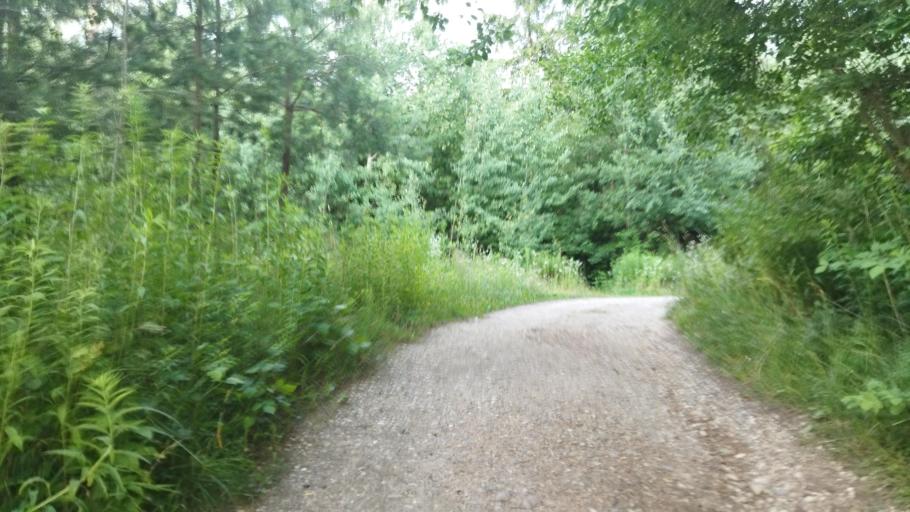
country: DE
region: Bavaria
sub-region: Upper Palatinate
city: Mintraching
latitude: 48.9645
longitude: 12.3002
